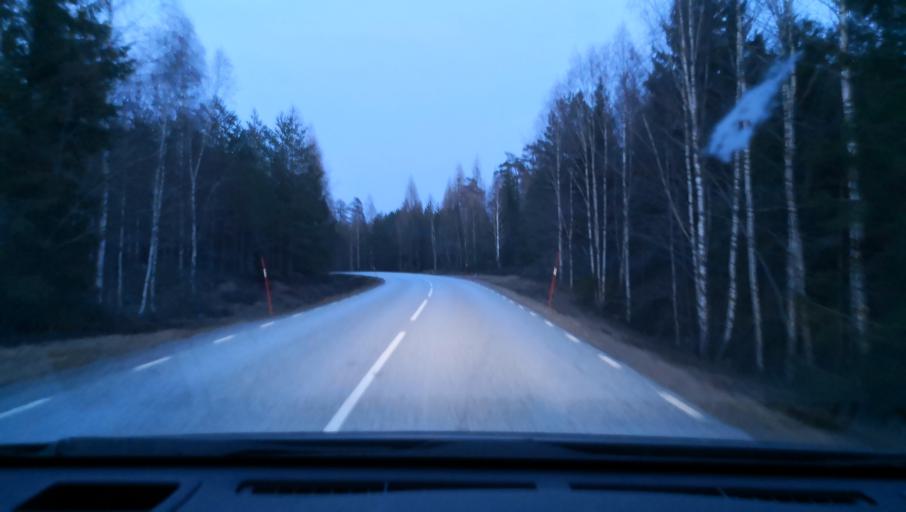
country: SE
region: OErebro
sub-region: Lindesbergs Kommun
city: Frovi
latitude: 59.5914
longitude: 15.4090
